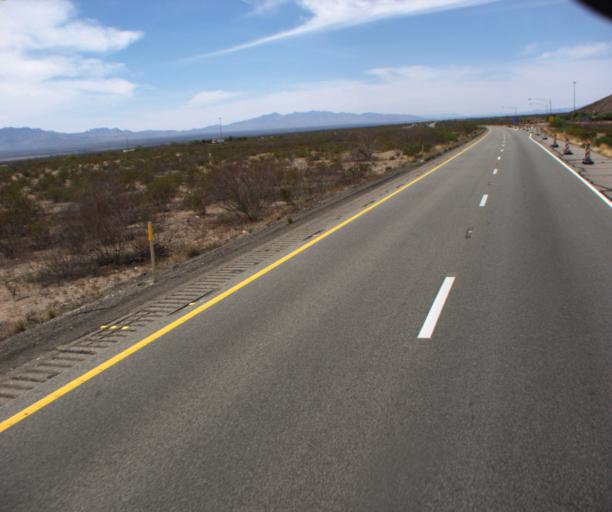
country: US
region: New Mexico
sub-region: Hidalgo County
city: Lordsburg
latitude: 32.2373
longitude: -109.0818
